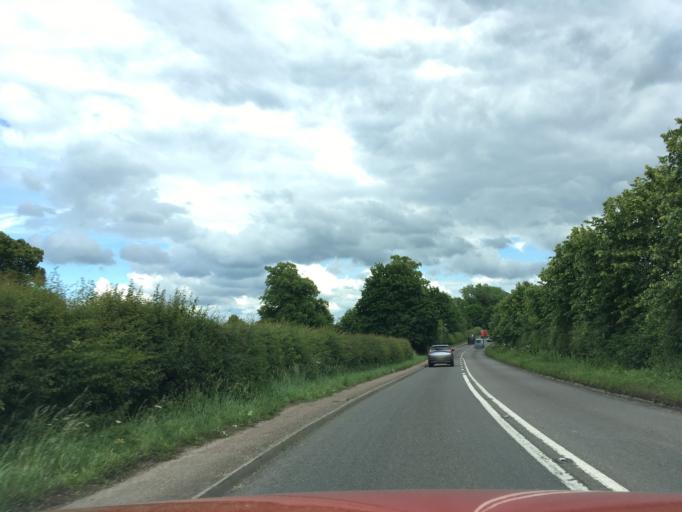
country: GB
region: England
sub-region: Central Bedfordshire
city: Woburn
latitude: 51.9933
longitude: -0.6248
